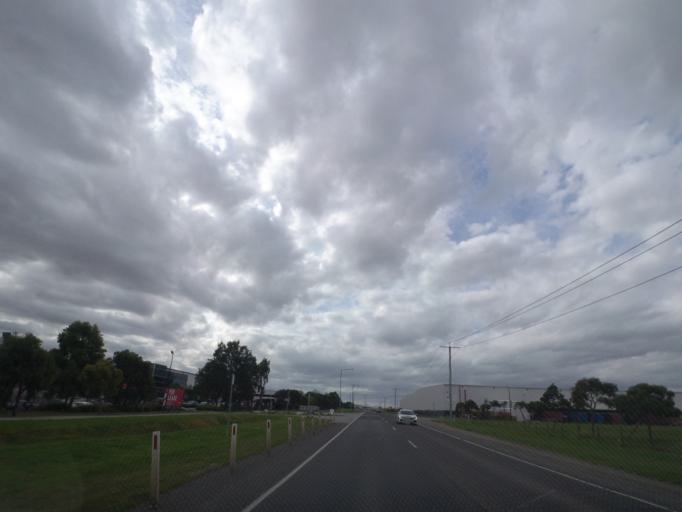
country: AU
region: Victoria
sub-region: Brimbank
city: Keilor Park
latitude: -37.7015
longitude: 144.8576
